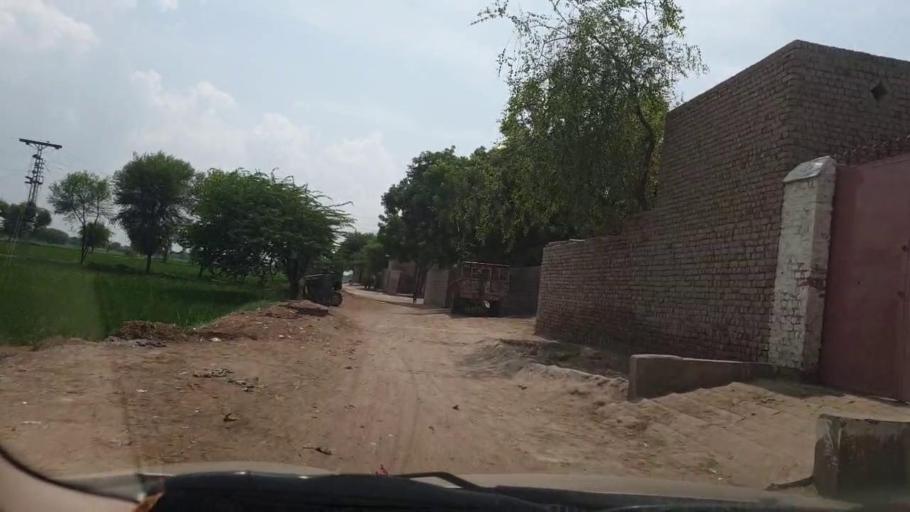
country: PK
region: Sindh
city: Larkana
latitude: 27.5922
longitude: 68.1214
